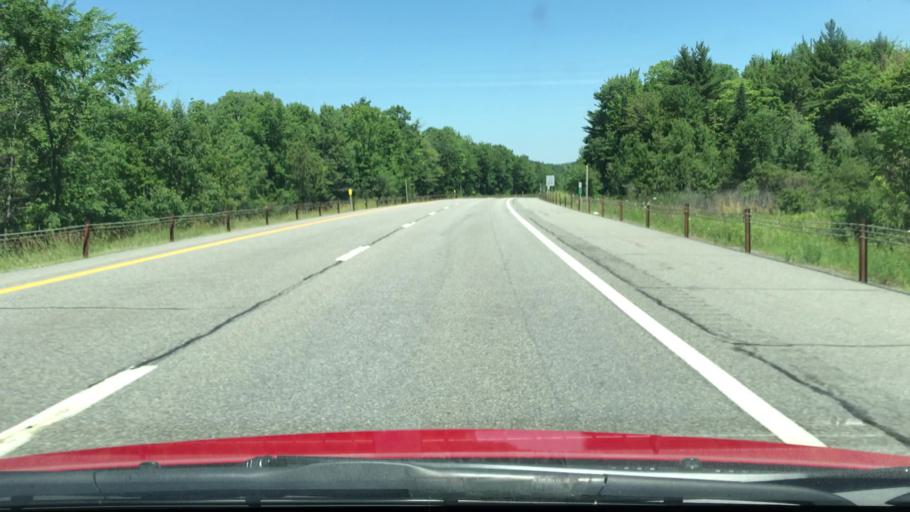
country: US
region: New York
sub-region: Essex County
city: Elizabethtown
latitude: 44.1691
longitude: -73.5837
